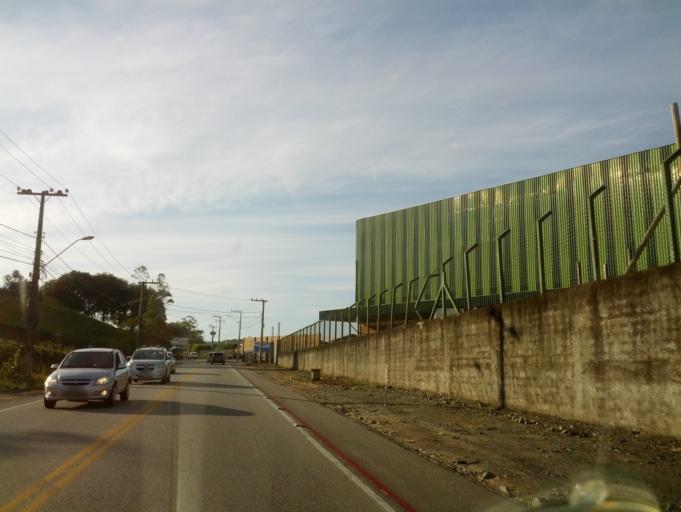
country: BR
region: Santa Catarina
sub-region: Indaial
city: Indaial
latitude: -26.8936
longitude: -49.1578
